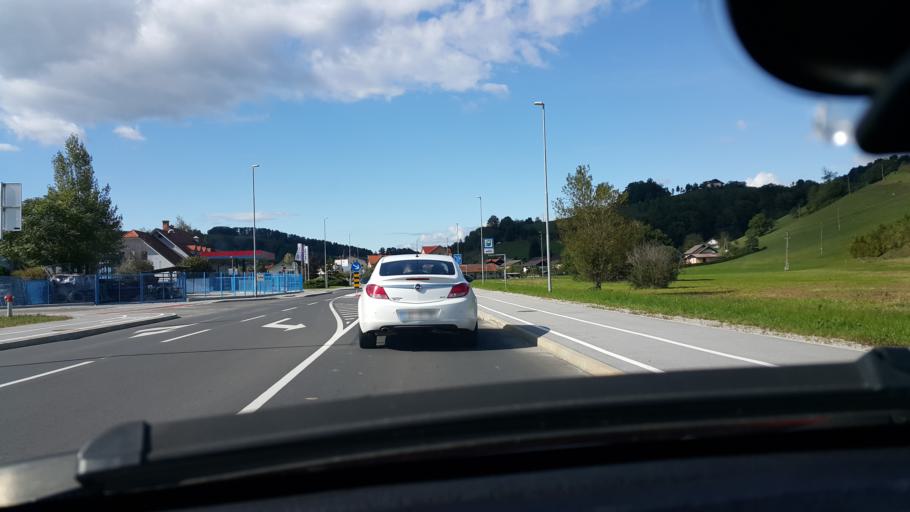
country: SI
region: Kungota
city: Zgornja Kungota
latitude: 46.6343
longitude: 15.6212
